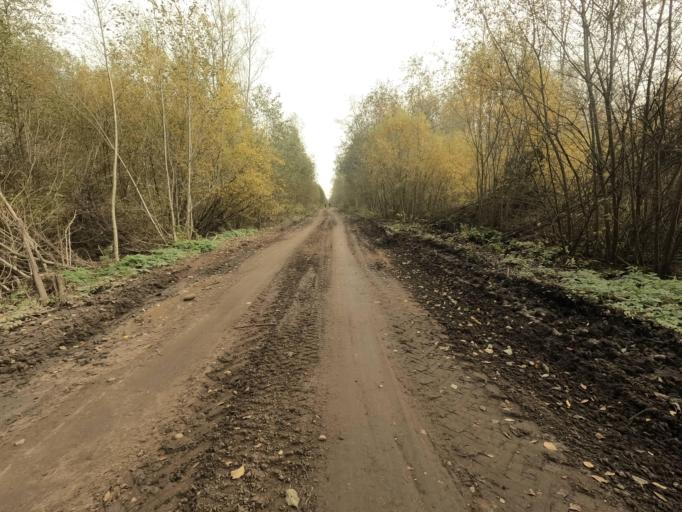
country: RU
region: Novgorod
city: Batetskiy
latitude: 58.8791
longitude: 30.7566
